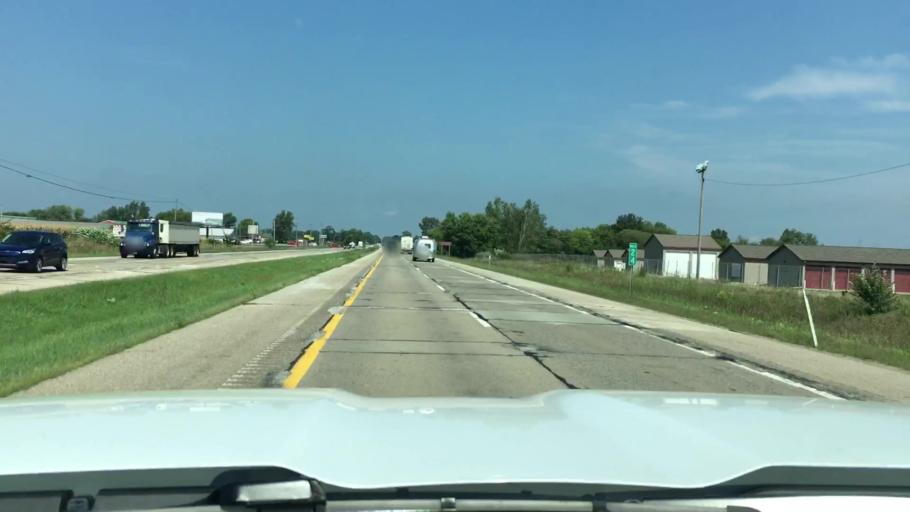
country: US
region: Michigan
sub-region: Kalamazoo County
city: Schoolcraft
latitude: 42.0932
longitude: -85.6367
